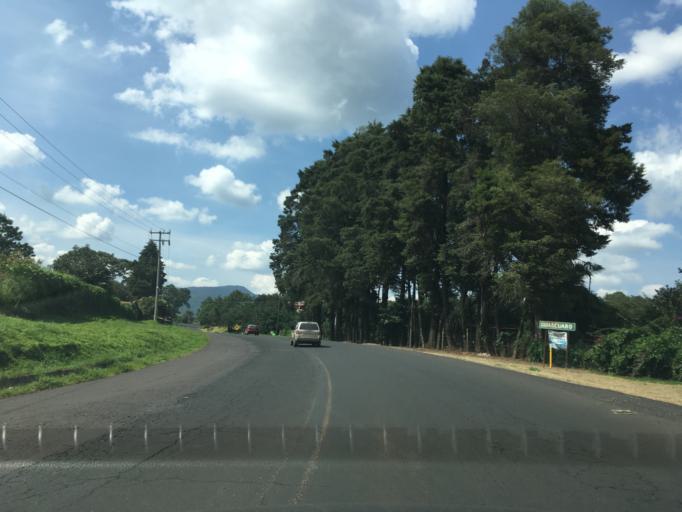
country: MX
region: Michoacan
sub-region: Tingueindin
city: Tingueindin
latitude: 19.7899
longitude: -102.5126
